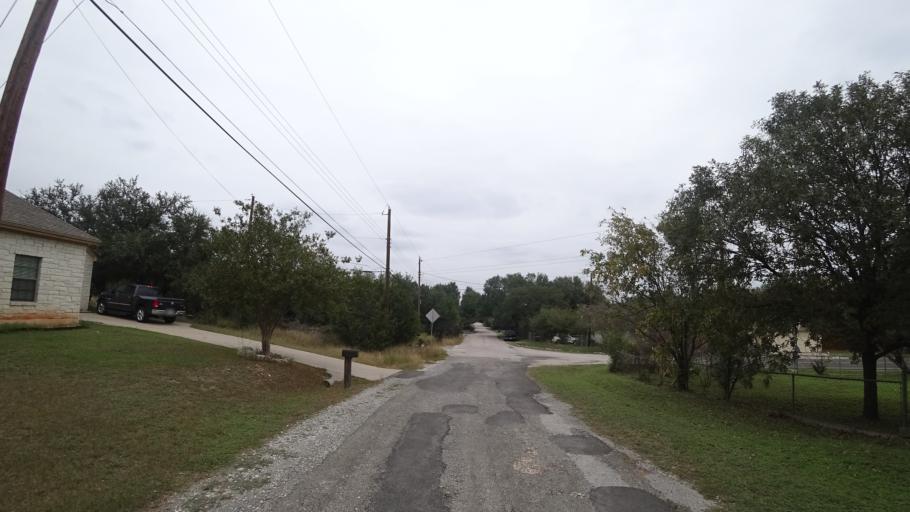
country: US
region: Texas
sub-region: Travis County
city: Lakeway
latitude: 30.3709
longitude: -97.9387
